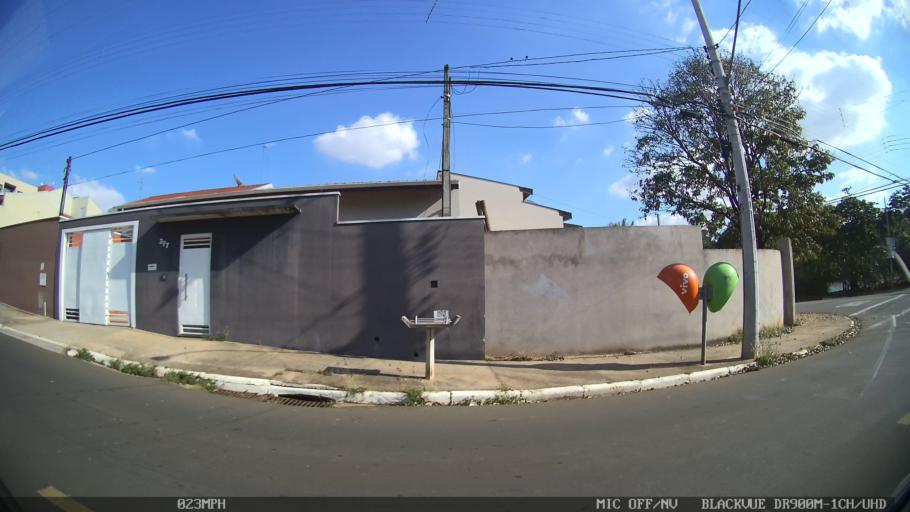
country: BR
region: Sao Paulo
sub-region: Nova Odessa
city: Nova Odessa
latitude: -22.7781
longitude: -47.3027
